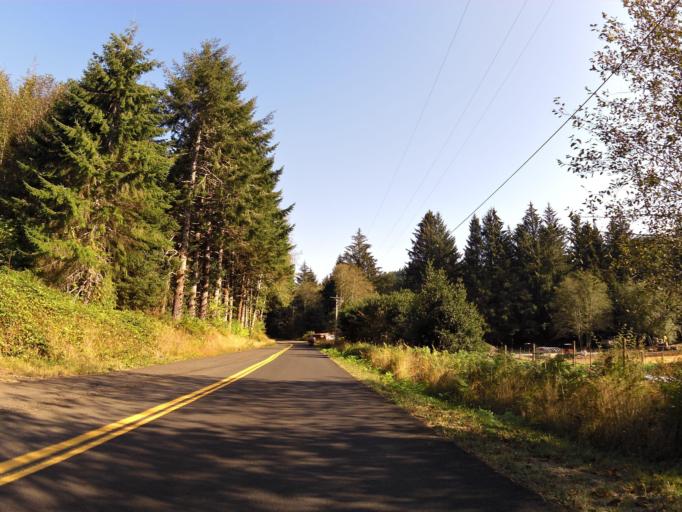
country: US
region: Oregon
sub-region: Lincoln County
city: Rose Lodge
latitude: 45.0765
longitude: -123.9362
